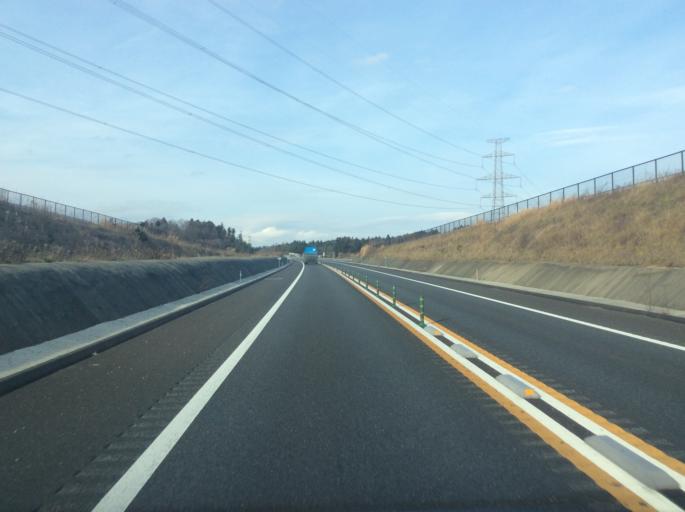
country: JP
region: Fukushima
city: Namie
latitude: 37.5142
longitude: 140.9437
